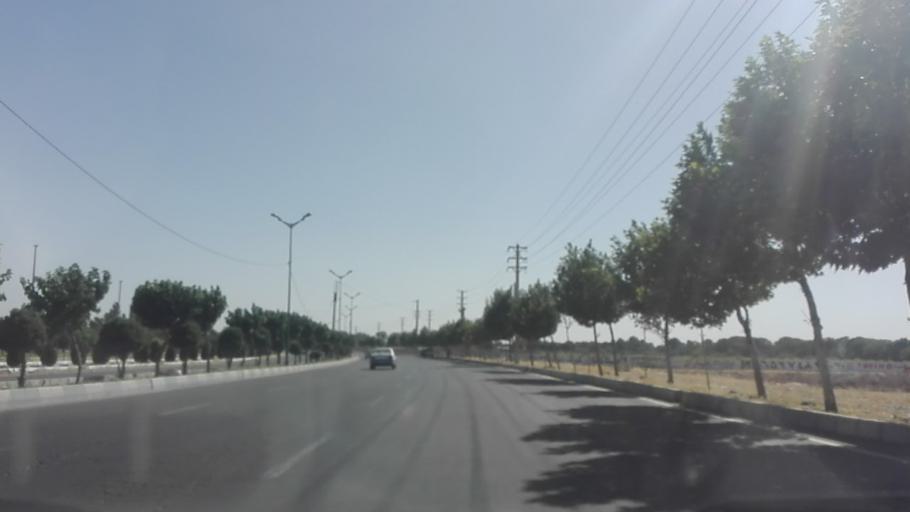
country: IR
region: Tehran
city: Shahriar
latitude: 35.6333
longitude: 51.0590
